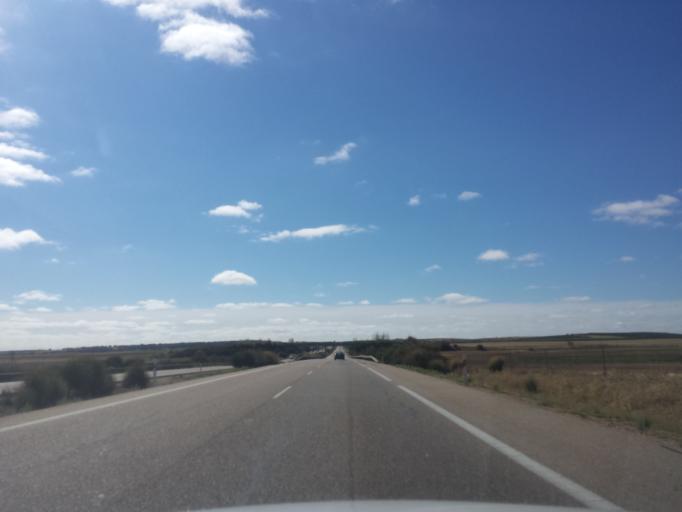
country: ES
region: Castille and Leon
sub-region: Provincia de Zamora
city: Villalpando
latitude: 41.8466
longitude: -5.3995
